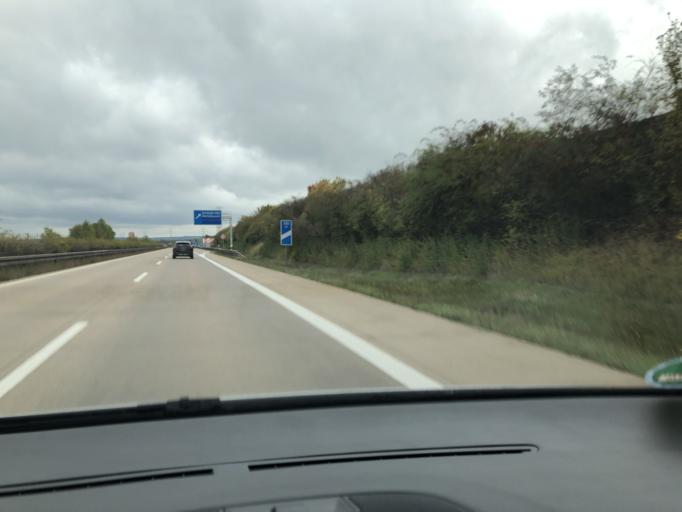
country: DE
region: Thuringia
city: Dornheim
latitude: 50.8212
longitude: 11.0037
